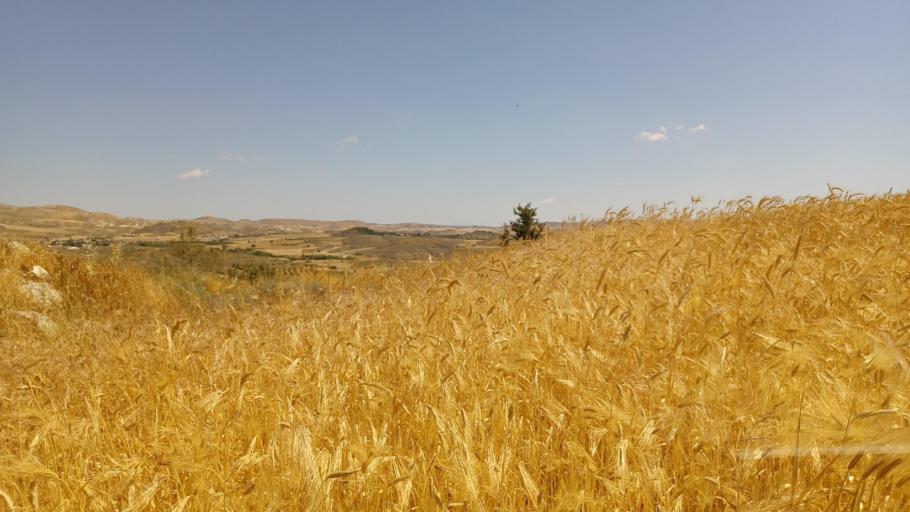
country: CY
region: Larnaka
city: Aradippou
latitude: 34.9939
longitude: 33.5696
